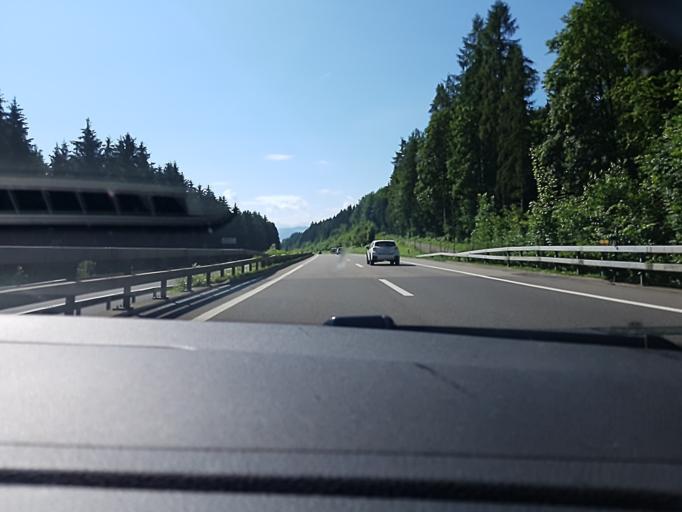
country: CH
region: Zurich
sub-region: Bezirk Horgen
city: Horgen / Scheller-Stockerstrasse
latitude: 47.2616
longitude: 8.5783
